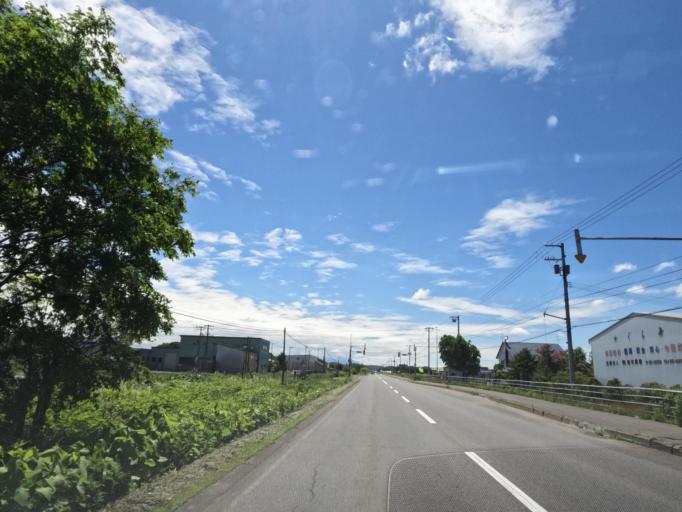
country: JP
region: Hokkaido
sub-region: Asahikawa-shi
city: Asahikawa
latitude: 43.7036
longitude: 142.3810
